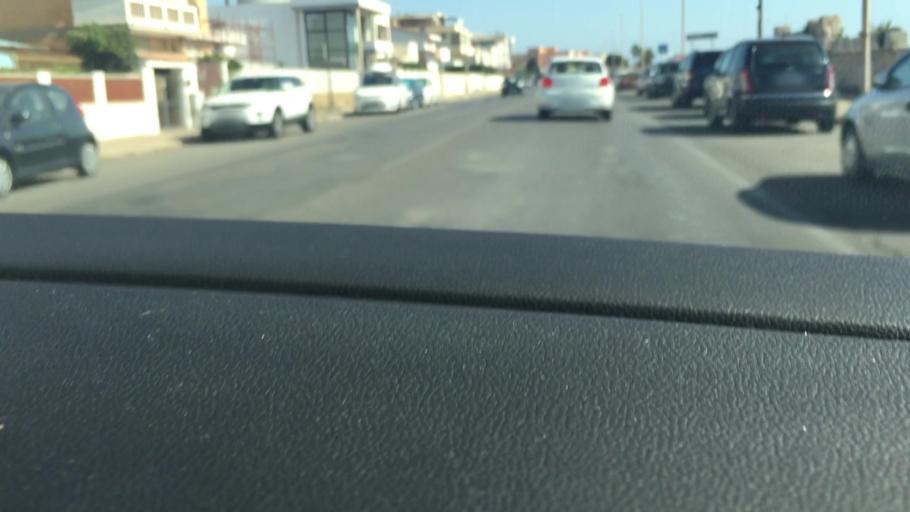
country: IT
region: Latium
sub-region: Citta metropolitana di Roma Capitale
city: Anzio
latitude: 41.4572
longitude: 12.6153
